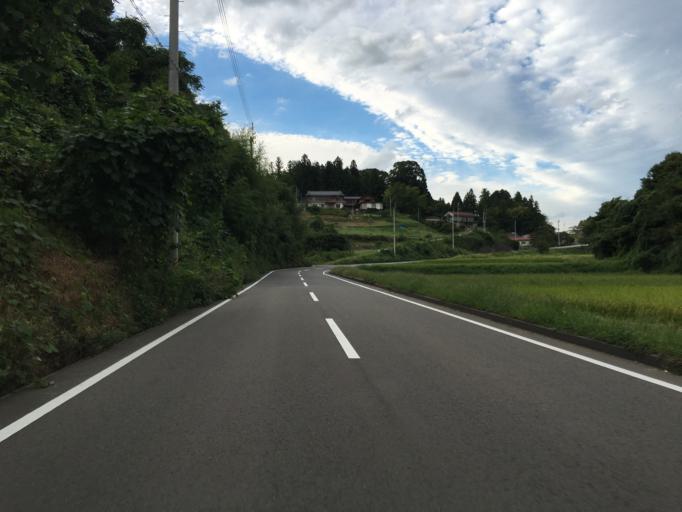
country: JP
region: Fukushima
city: Nihommatsu
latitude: 37.6034
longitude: 140.4969
